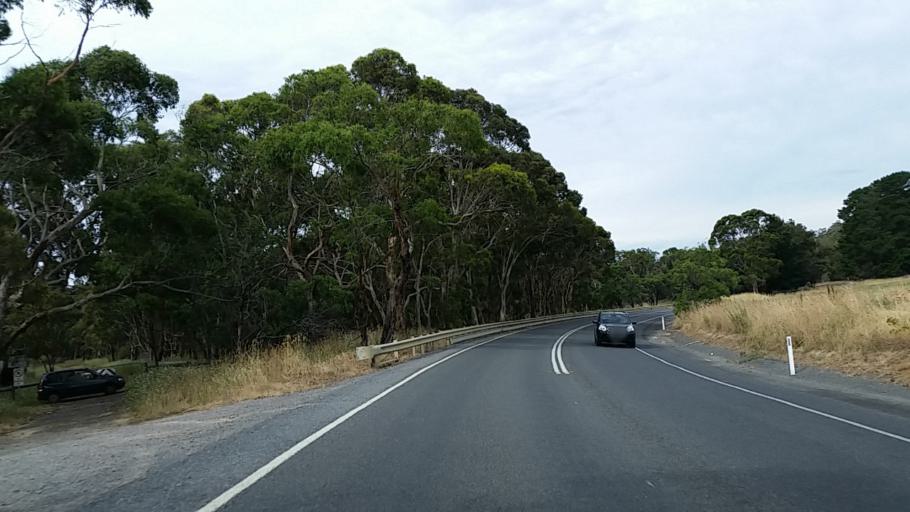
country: AU
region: South Australia
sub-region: Yankalilla
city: Normanville
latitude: -35.4138
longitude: 138.4314
